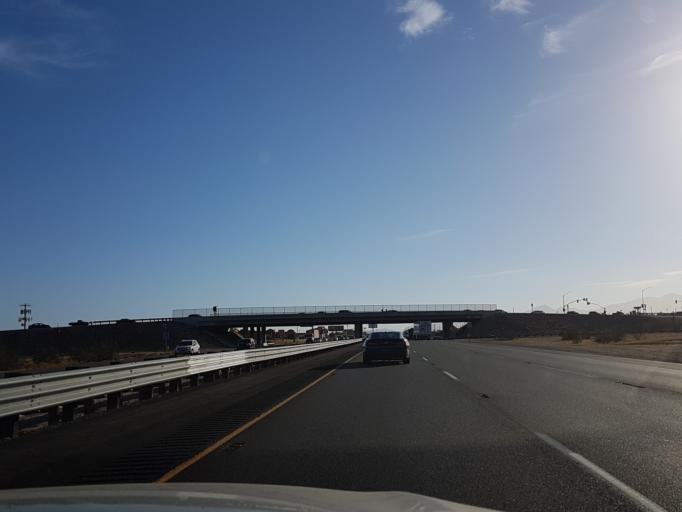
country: US
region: California
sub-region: San Bernardino County
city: Mountain View Acres
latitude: 34.4722
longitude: -117.3450
